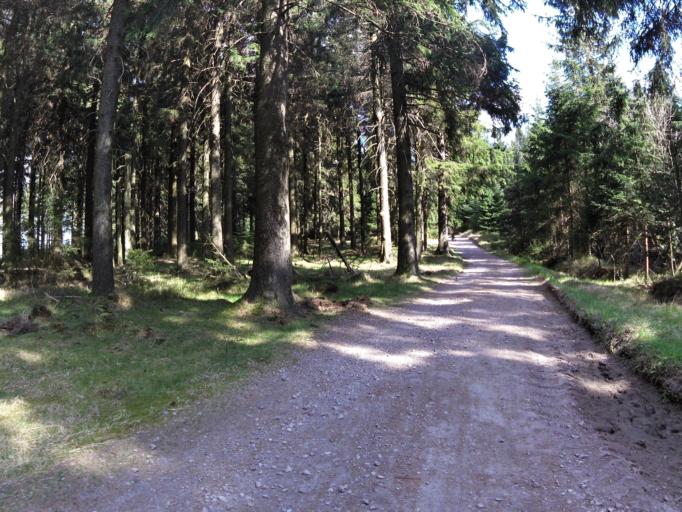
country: DE
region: Thuringia
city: Bermbach
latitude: 50.7153
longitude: 10.6511
